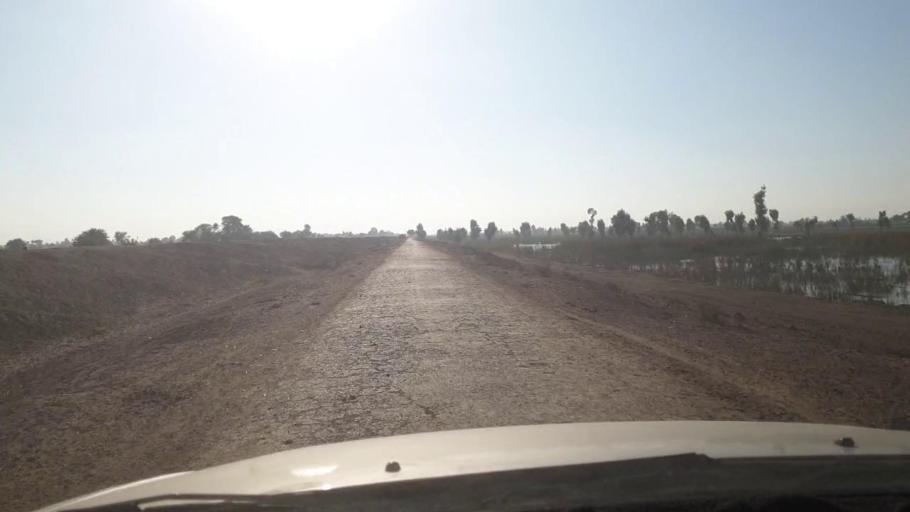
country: PK
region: Sindh
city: Ghotki
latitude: 28.0450
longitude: 69.3020
